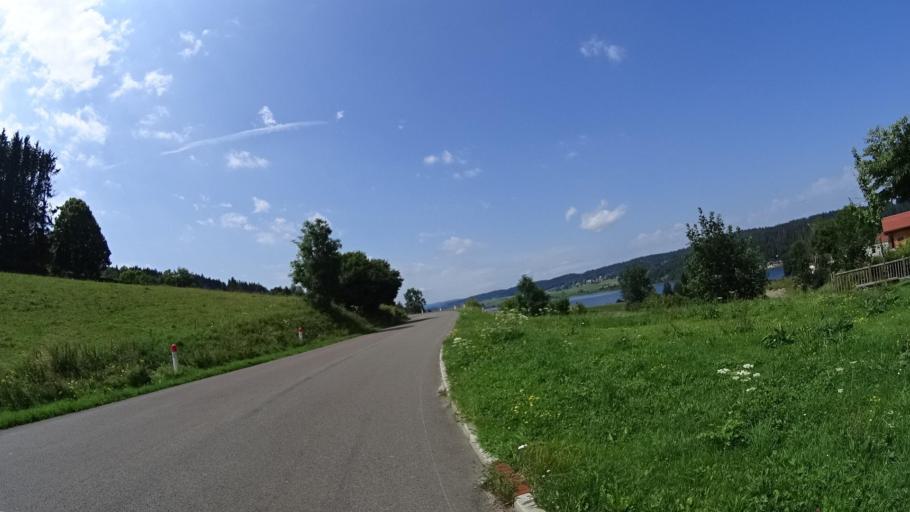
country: FR
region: Franche-Comte
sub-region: Departement du Doubs
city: Les Fourgs
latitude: 46.8358
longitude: 6.3453
